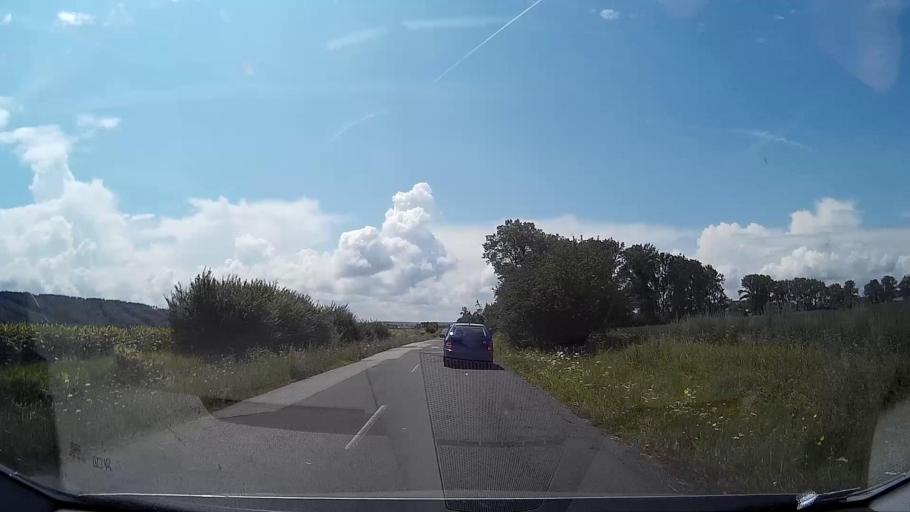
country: SK
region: Banskobystricky
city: Fil'akovo
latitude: 48.3362
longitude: 19.8238
